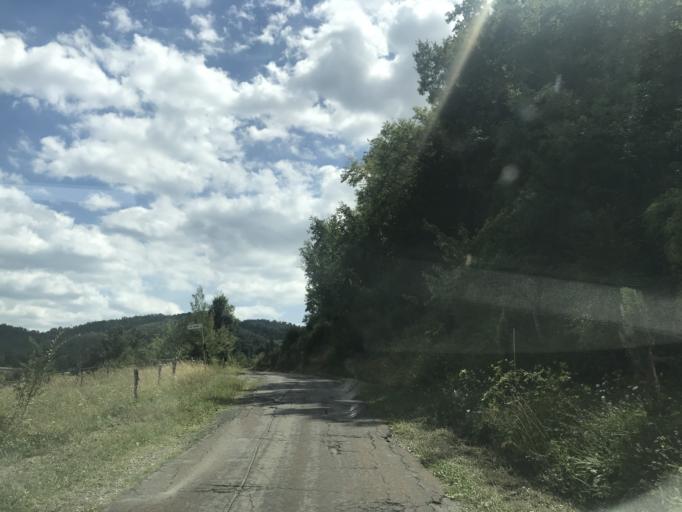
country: IT
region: Emilia-Romagna
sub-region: Provincia di Bologna
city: Grizzana Morandi
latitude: 44.2424
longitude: 11.1176
